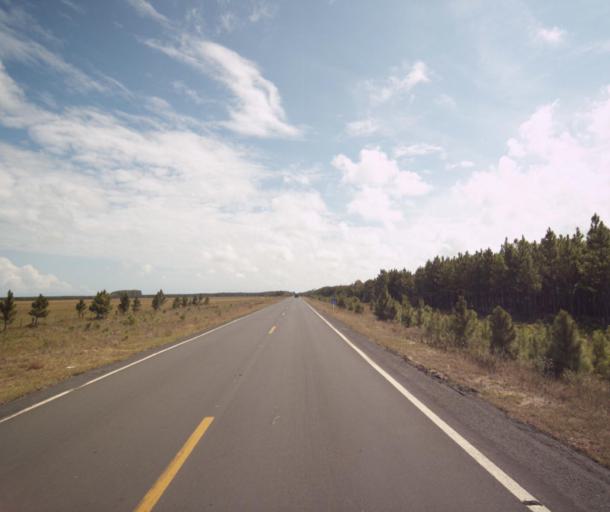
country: BR
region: Rio Grande do Sul
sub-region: Sao Lourenco Do Sul
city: Sao Lourenco do Sul
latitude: -31.4510
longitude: -51.2131
